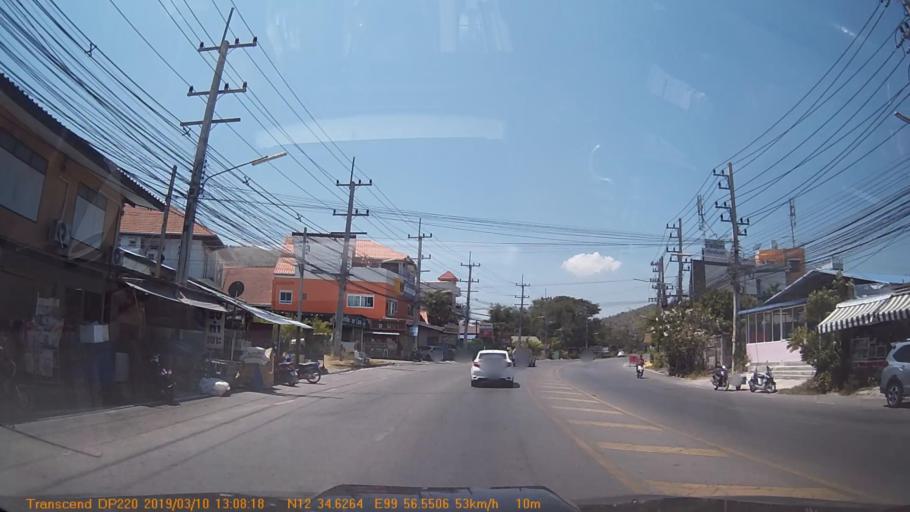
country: TH
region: Prachuap Khiri Khan
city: Hua Hin
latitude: 12.5772
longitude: 99.9423
